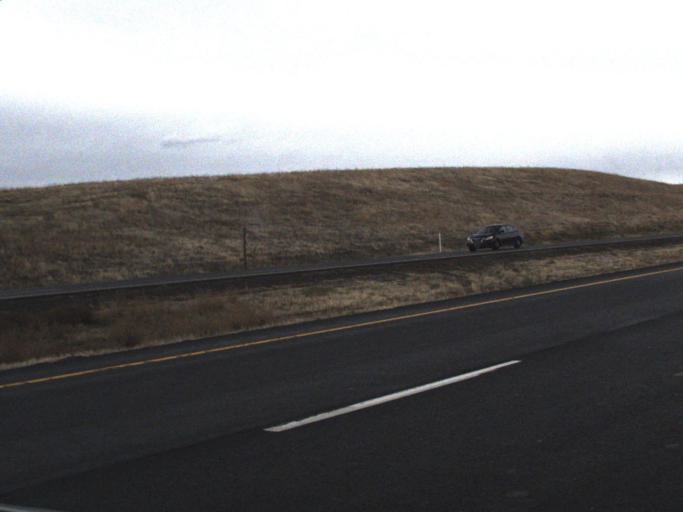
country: US
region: Washington
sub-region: Walla Walla County
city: Garrett
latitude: 46.0557
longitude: -118.4512
